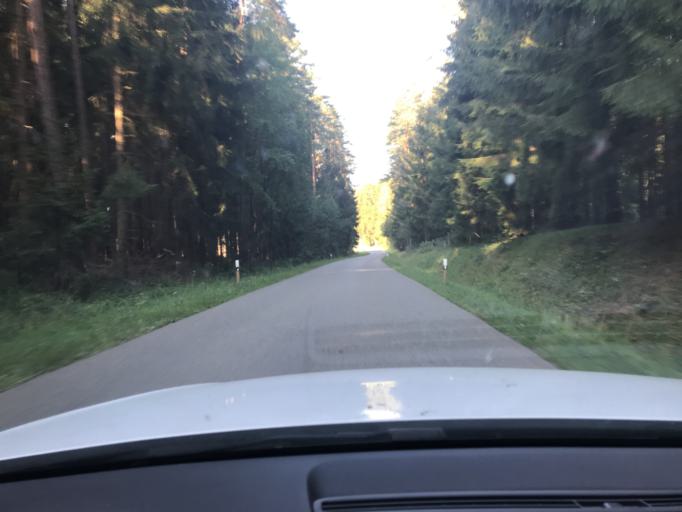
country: DE
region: Bavaria
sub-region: Upper Palatinate
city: Auerbach
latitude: 49.7152
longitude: 11.6013
